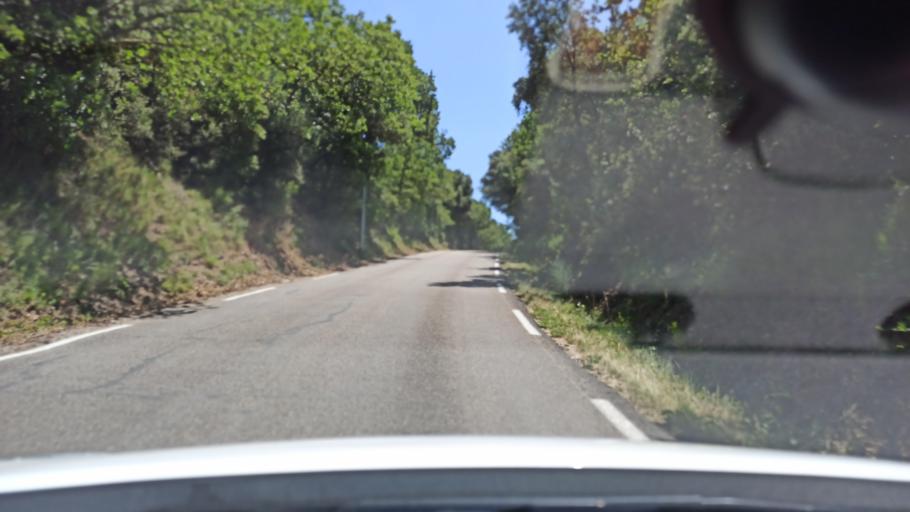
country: FR
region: Provence-Alpes-Cote d'Azur
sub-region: Departement du Vaucluse
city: Caumont-sur-Durance
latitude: 43.9054
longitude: 4.9273
